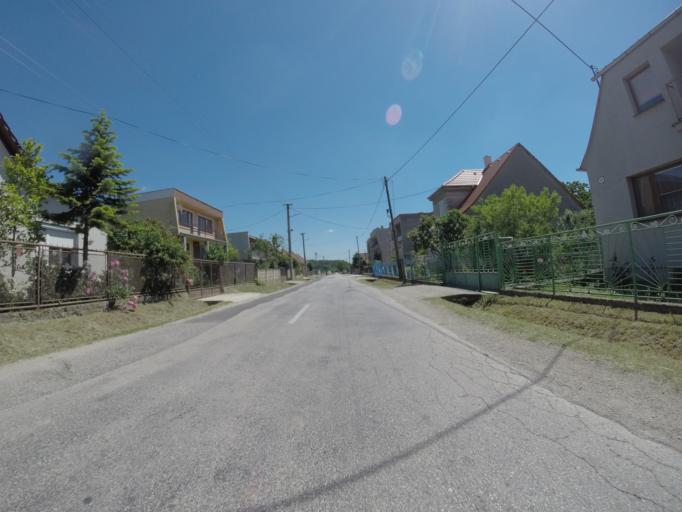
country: SK
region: Trnavsky
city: Hlohovec
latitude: 48.4881
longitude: 17.8829
